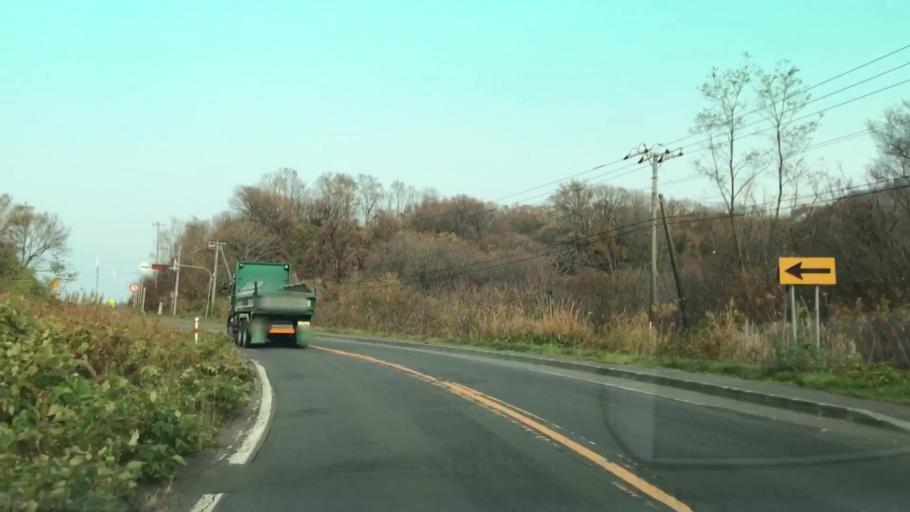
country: JP
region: Hokkaido
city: Ishikari
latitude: 43.4137
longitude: 141.4325
